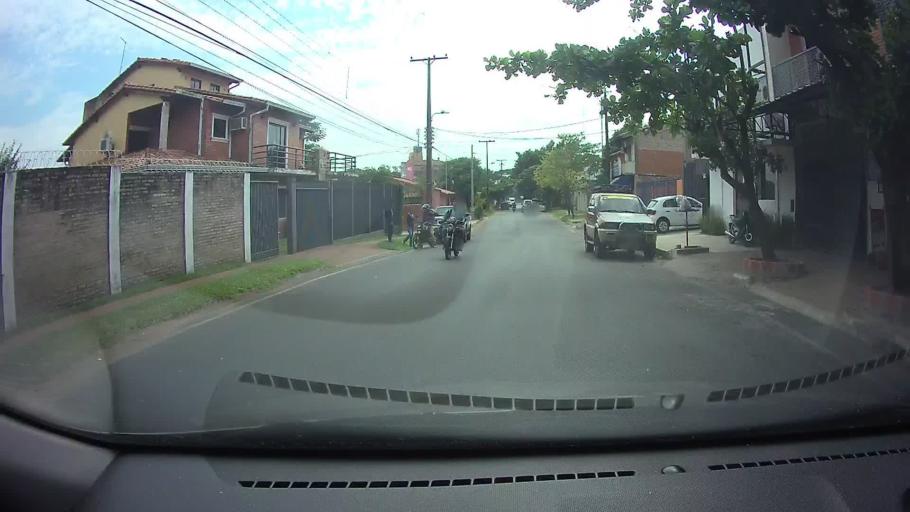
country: PY
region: Central
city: Fernando de la Mora
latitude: -25.3028
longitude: -57.5416
